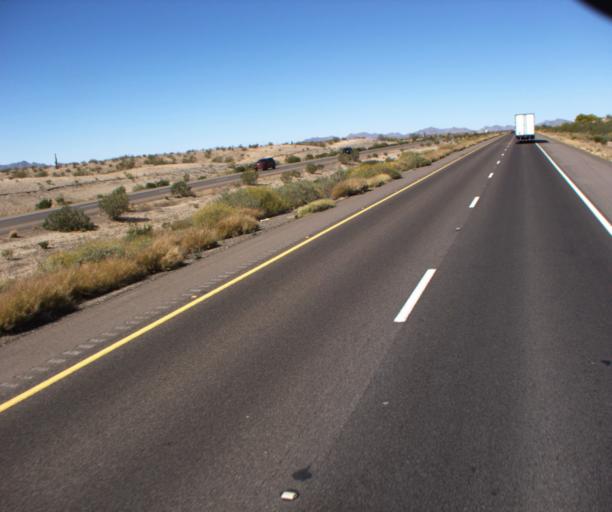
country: US
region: Arizona
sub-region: Maricopa County
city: Gila Bend
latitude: 33.0901
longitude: -112.6481
